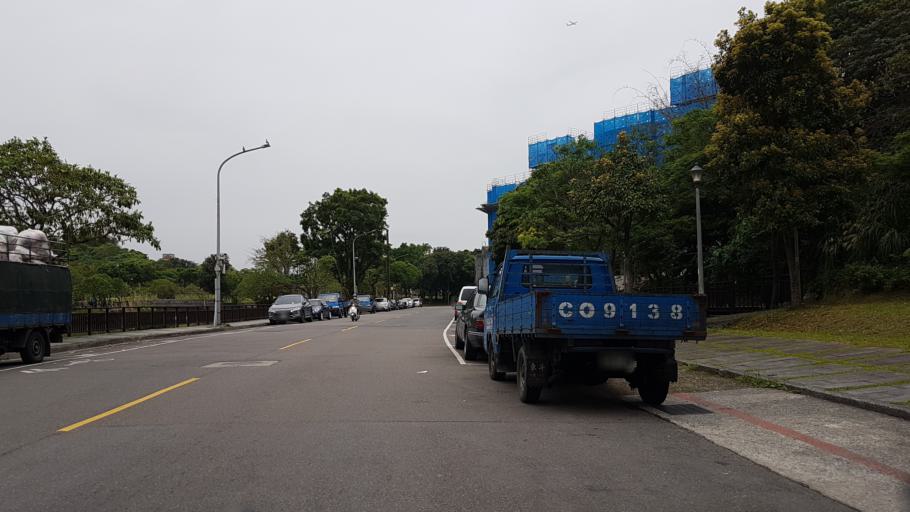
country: TW
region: Taipei
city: Taipei
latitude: 25.0423
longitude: 121.5929
